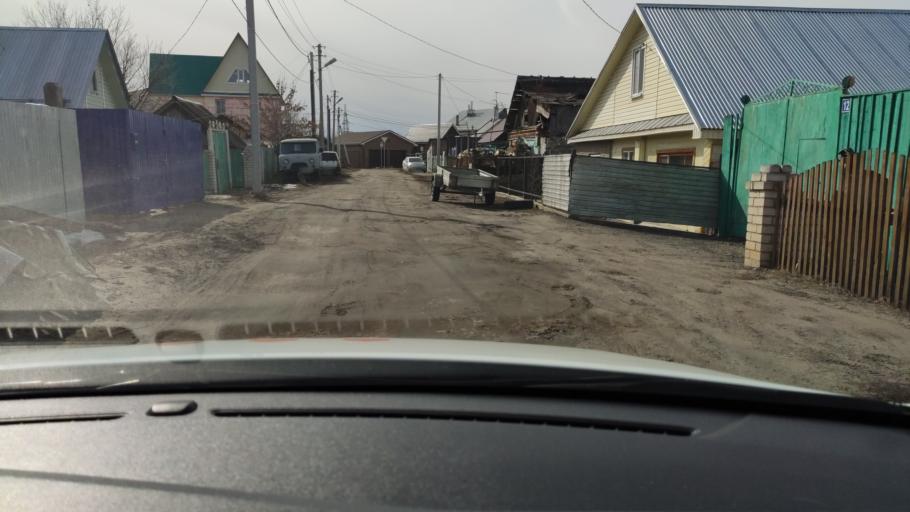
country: RU
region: Tatarstan
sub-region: Gorod Kazan'
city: Kazan
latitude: 55.7261
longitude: 49.1415
